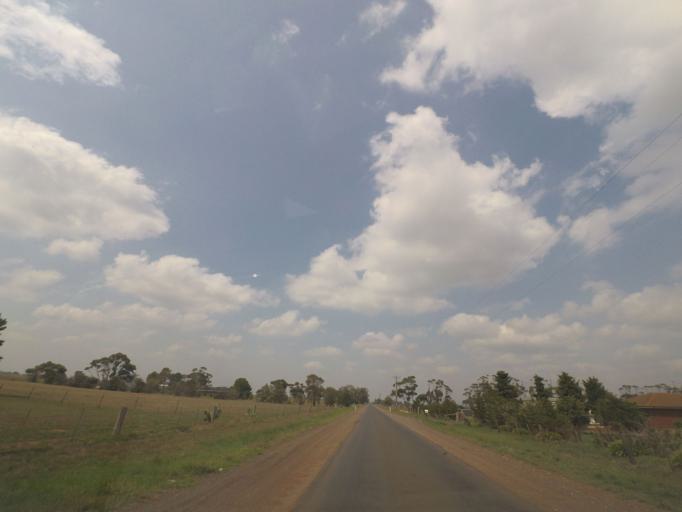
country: AU
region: Victoria
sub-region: Melton
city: Melton West
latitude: -37.6538
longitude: 144.5557
